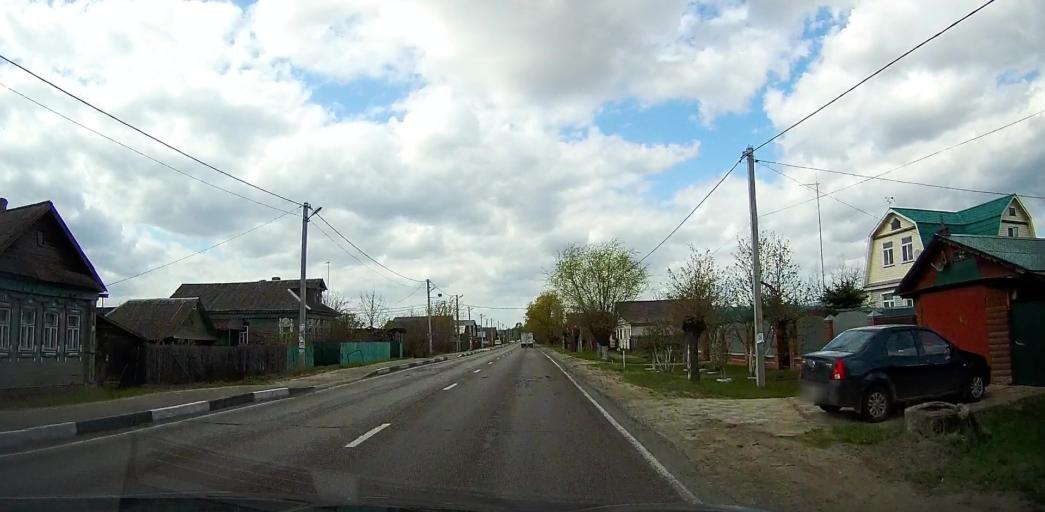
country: RU
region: Moskovskaya
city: Davydovo
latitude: 55.6381
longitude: 38.8657
